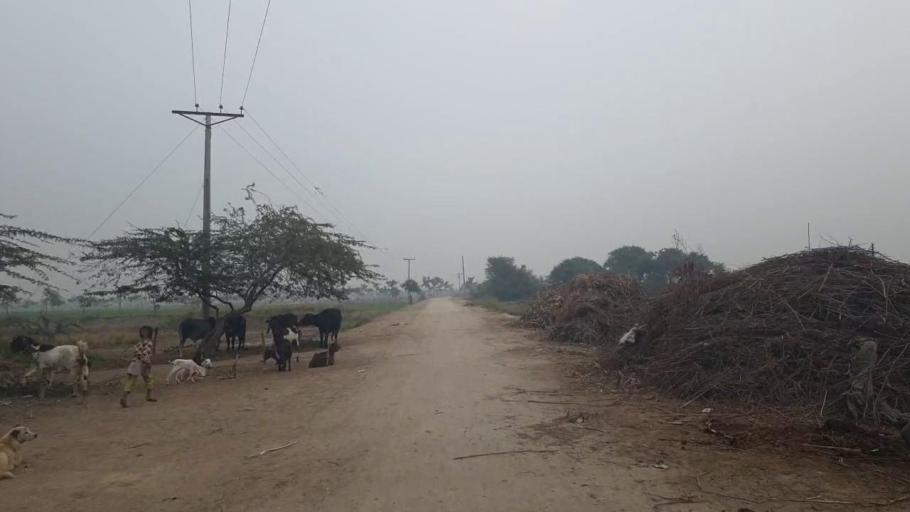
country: PK
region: Sindh
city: Tando Adam
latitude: 25.7481
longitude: 68.6728
